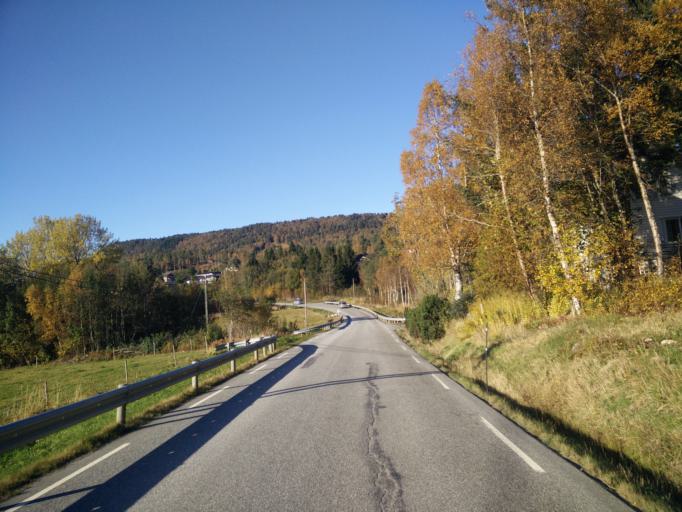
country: NO
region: More og Romsdal
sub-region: Halsa
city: Liaboen
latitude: 63.1147
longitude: 8.3212
